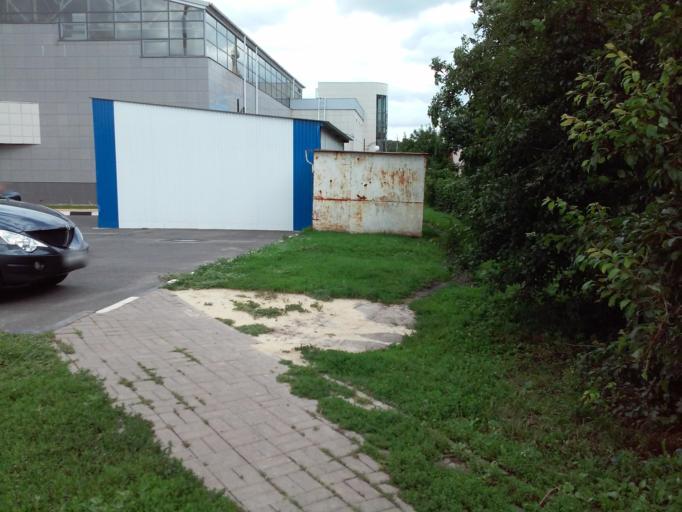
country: RU
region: Belgorod
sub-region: Belgorodskiy Rayon
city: Belgorod
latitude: 50.5364
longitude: 36.5831
